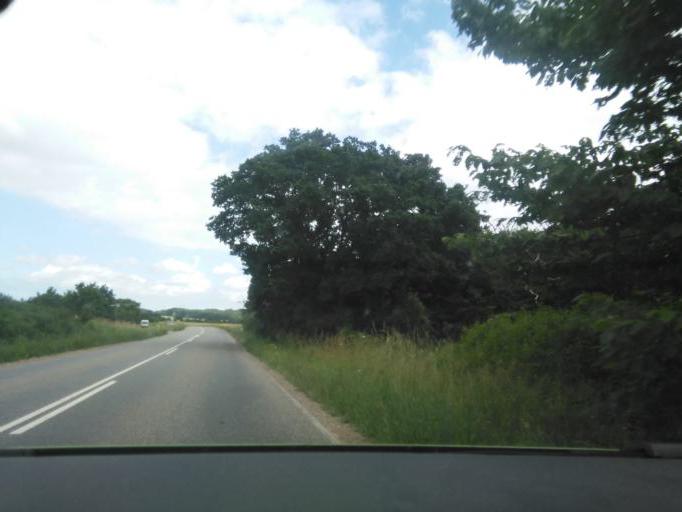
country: DK
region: Zealand
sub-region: Kalundborg Kommune
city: Hong
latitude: 55.5592
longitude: 11.3127
